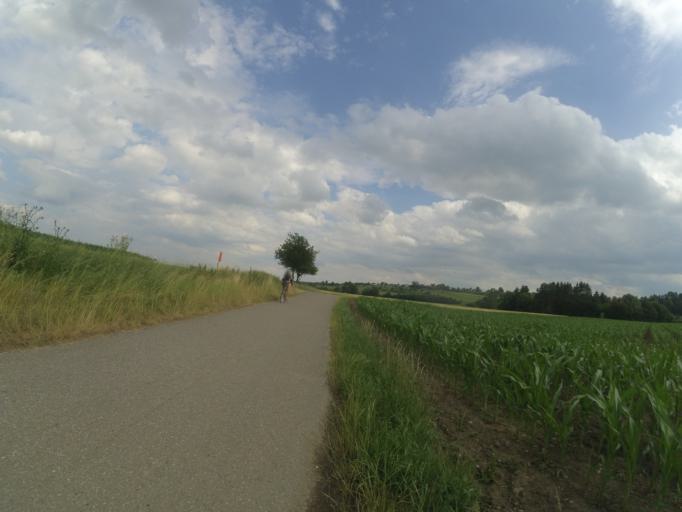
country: DE
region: Baden-Wuerttemberg
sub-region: Tuebingen Region
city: Griesingen
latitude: 48.2741
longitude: 9.7666
